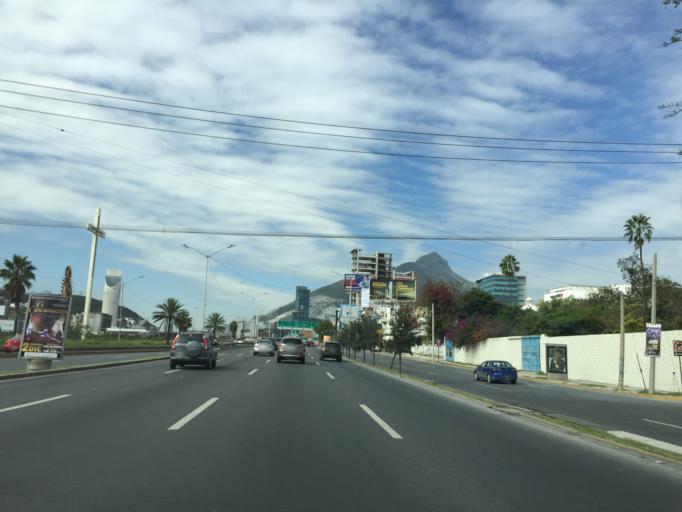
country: MX
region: Nuevo Leon
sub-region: Monterrey
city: Monterrey
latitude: 25.6695
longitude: -100.3421
